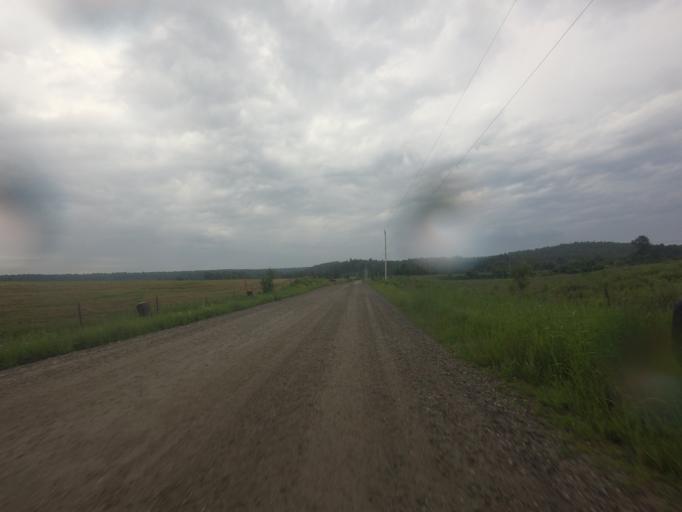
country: CA
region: Quebec
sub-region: Outaouais
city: Maniwaki
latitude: 46.4506
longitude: -75.9431
